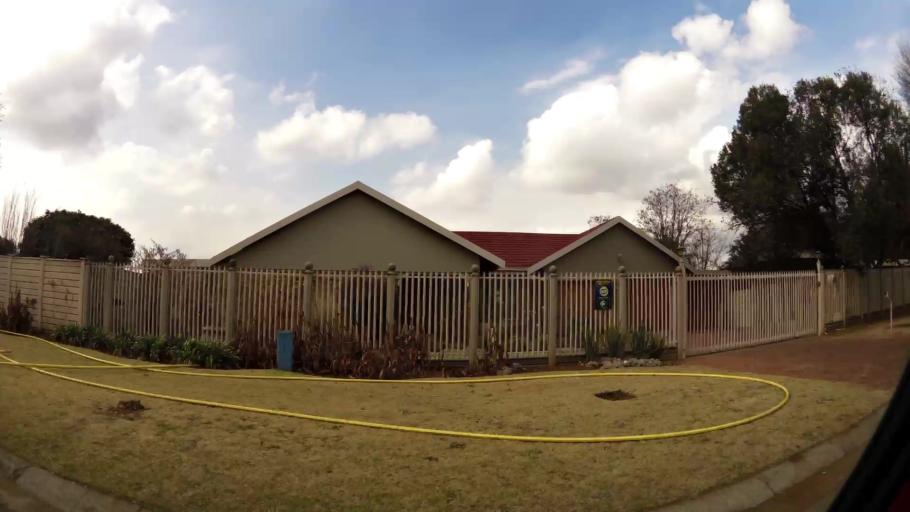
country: ZA
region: Gauteng
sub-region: Sedibeng District Municipality
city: Vanderbijlpark
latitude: -26.7261
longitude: 27.8477
